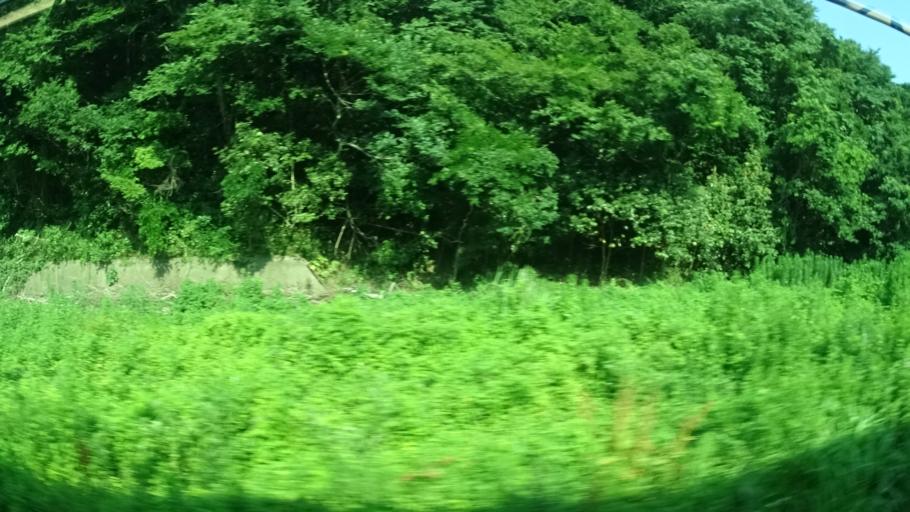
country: JP
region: Fukushima
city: Iwaki
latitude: 37.1892
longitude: 141.0001
